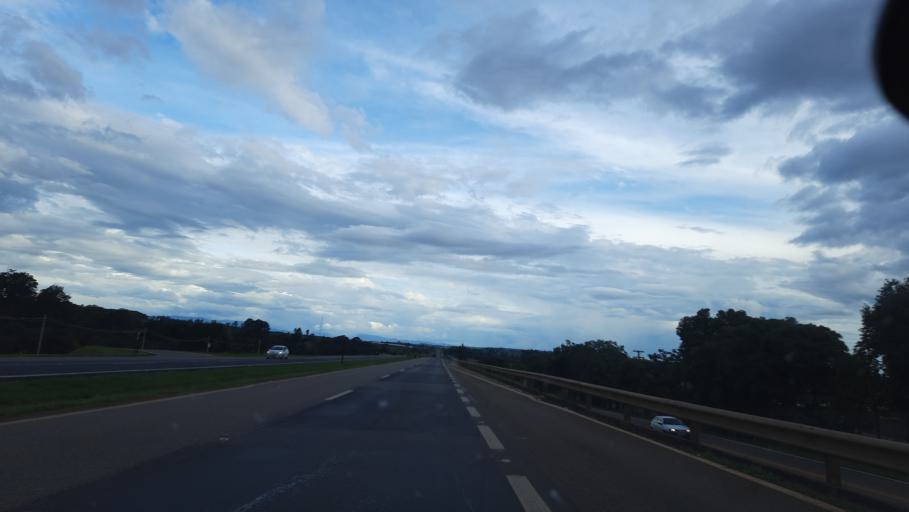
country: BR
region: Sao Paulo
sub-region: Casa Branca
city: Casa Branca
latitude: -21.7701
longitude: -47.0663
